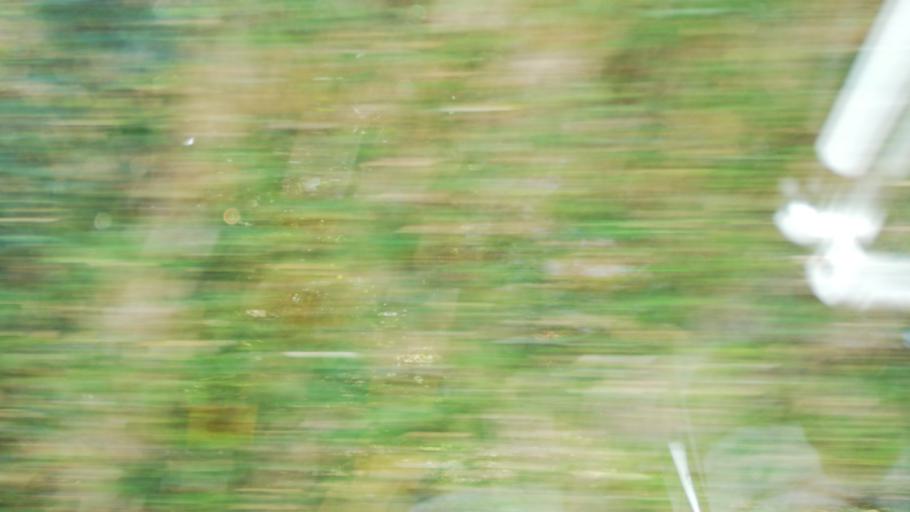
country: MU
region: Moka
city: Moka
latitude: -20.2283
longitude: 57.4755
